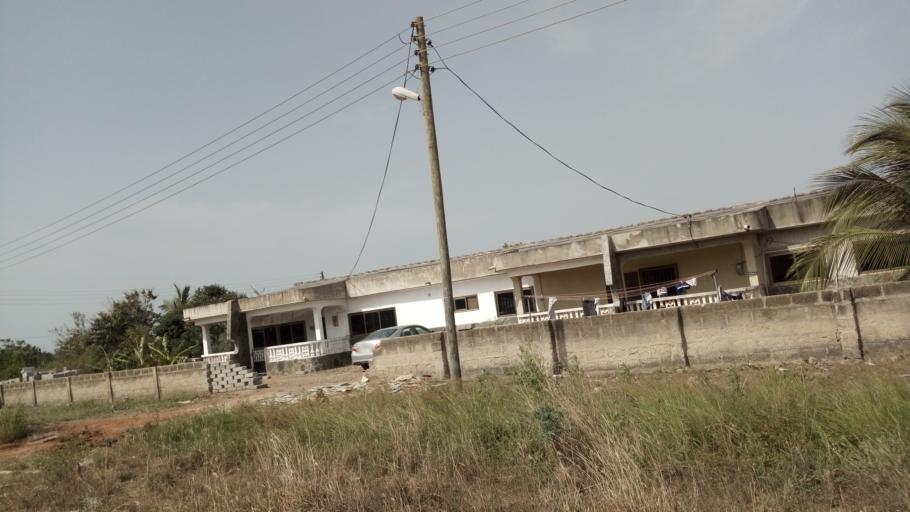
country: GH
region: Central
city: Winneba
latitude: 5.3740
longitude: -0.6496
